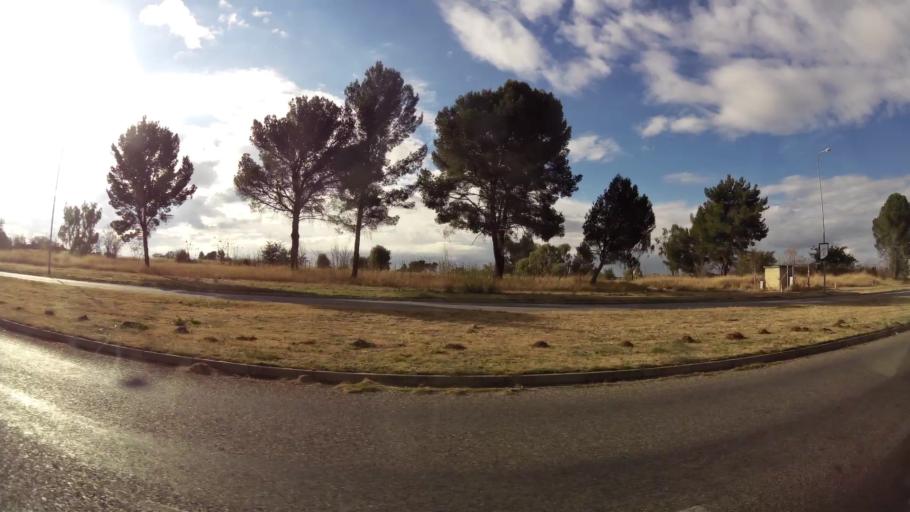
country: ZA
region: Orange Free State
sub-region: Lejweleputswa District Municipality
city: Welkom
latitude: -27.9748
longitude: 26.7064
